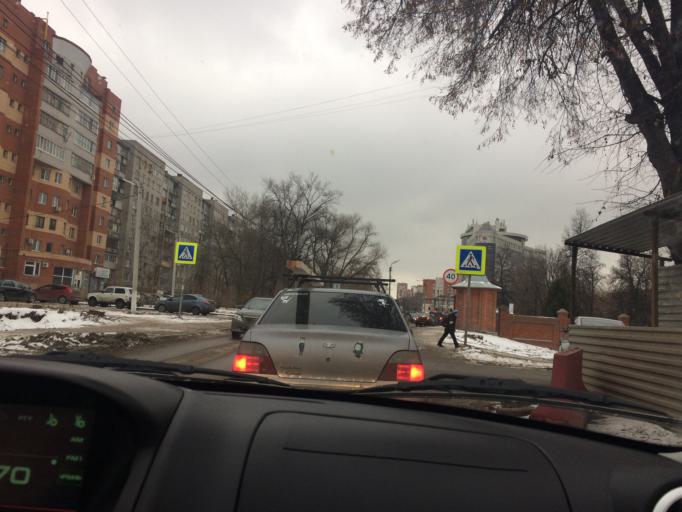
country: RU
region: Rjazan
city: Ryazan'
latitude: 54.6214
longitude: 39.7304
